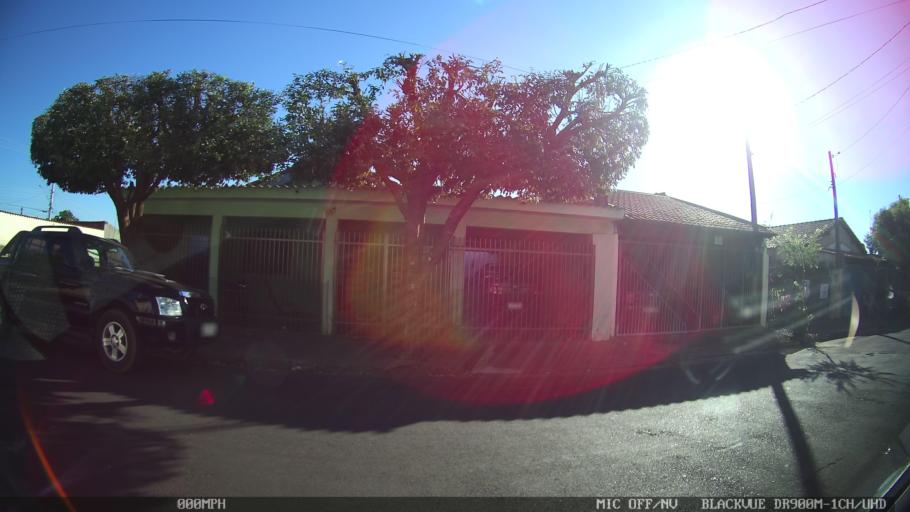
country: BR
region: Sao Paulo
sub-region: Olimpia
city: Olimpia
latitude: -20.7252
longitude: -48.9079
